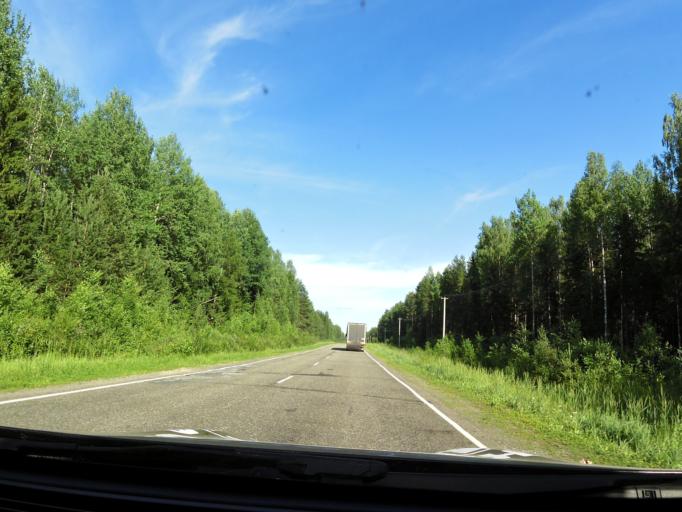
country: RU
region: Kirov
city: Belaya Kholunitsa
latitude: 58.9180
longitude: 51.1354
